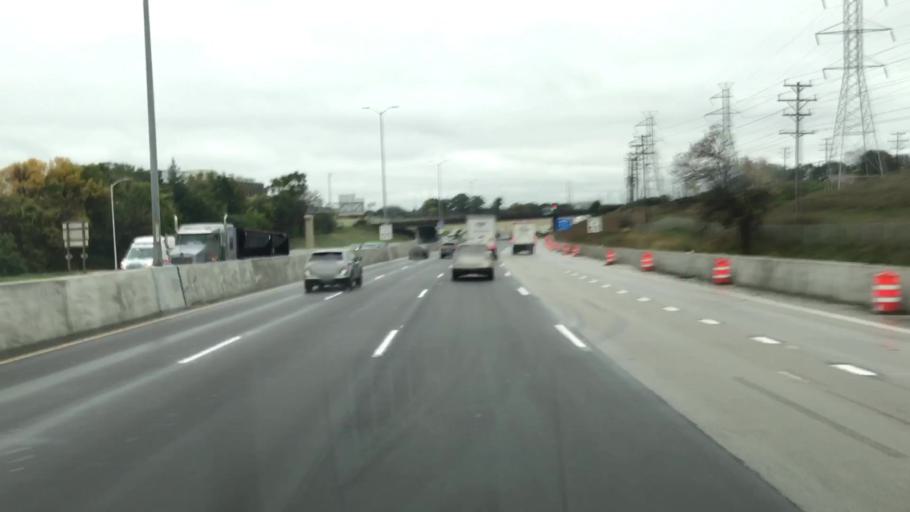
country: US
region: Wisconsin
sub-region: Milwaukee County
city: West Allis
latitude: 43.0003
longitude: -88.0382
